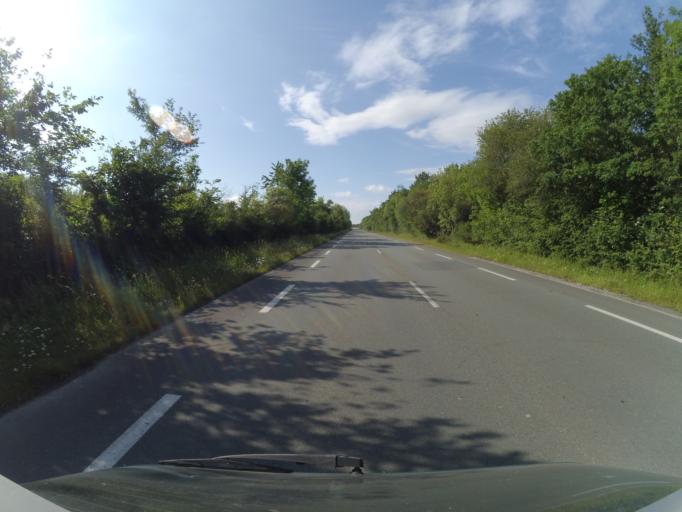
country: FR
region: Poitou-Charentes
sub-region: Departement de la Charente-Maritime
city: Saint-Agnant
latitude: 45.8262
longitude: -0.9345
